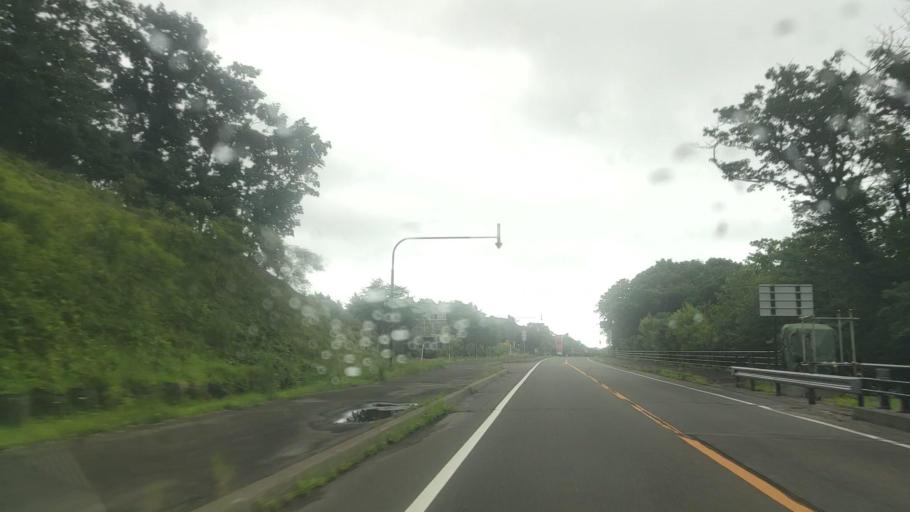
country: JP
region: Hokkaido
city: Shiraoi
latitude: 42.4780
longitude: 141.1462
